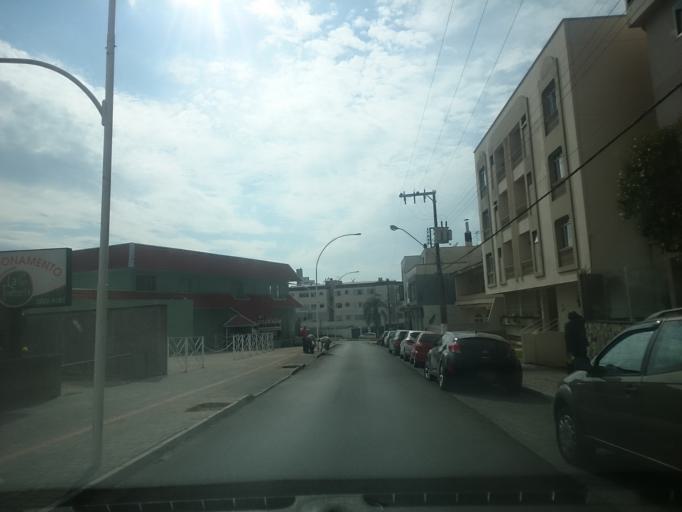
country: BR
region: Santa Catarina
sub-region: Lages
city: Lages
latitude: -27.8110
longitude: -50.3220
